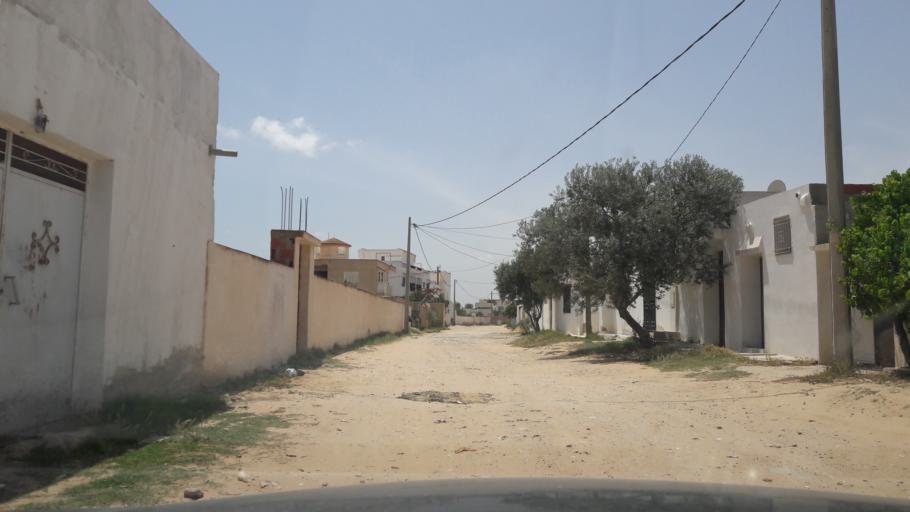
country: TN
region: Safaqis
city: Al Qarmadah
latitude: 34.7805
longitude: 10.7575
